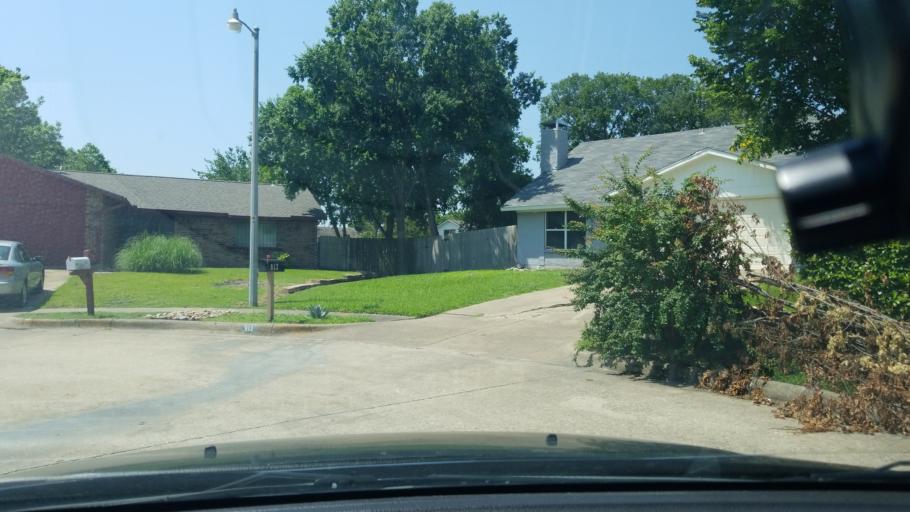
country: US
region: Texas
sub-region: Dallas County
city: Sunnyvale
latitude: 32.8275
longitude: -96.6095
